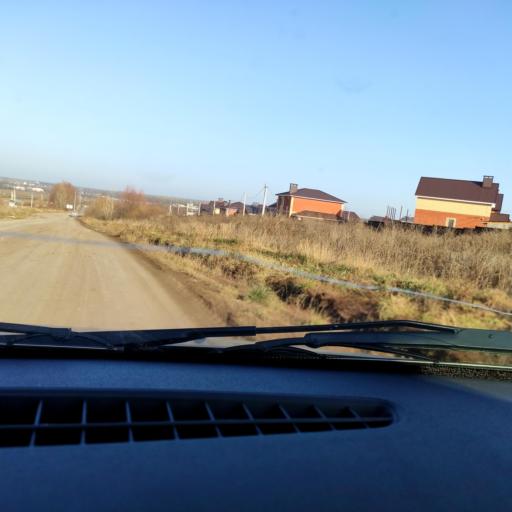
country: RU
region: Bashkortostan
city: Kabakovo
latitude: 54.6348
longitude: 56.0739
